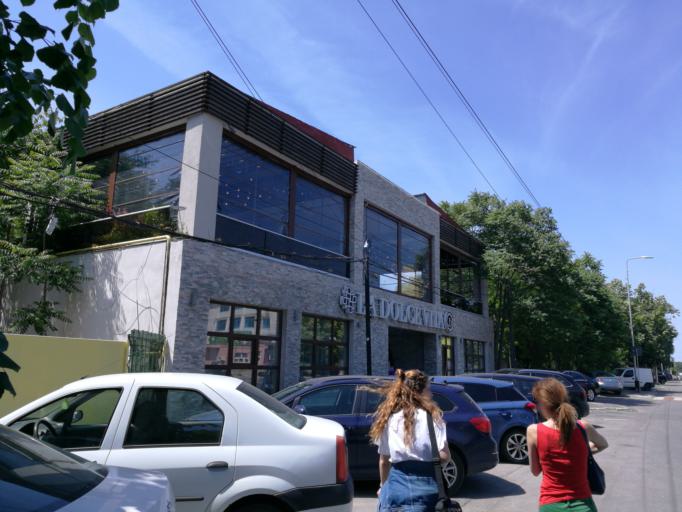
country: RO
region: Constanta
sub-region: Municipiul Constanta
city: Constanta
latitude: 44.2084
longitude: 28.6433
